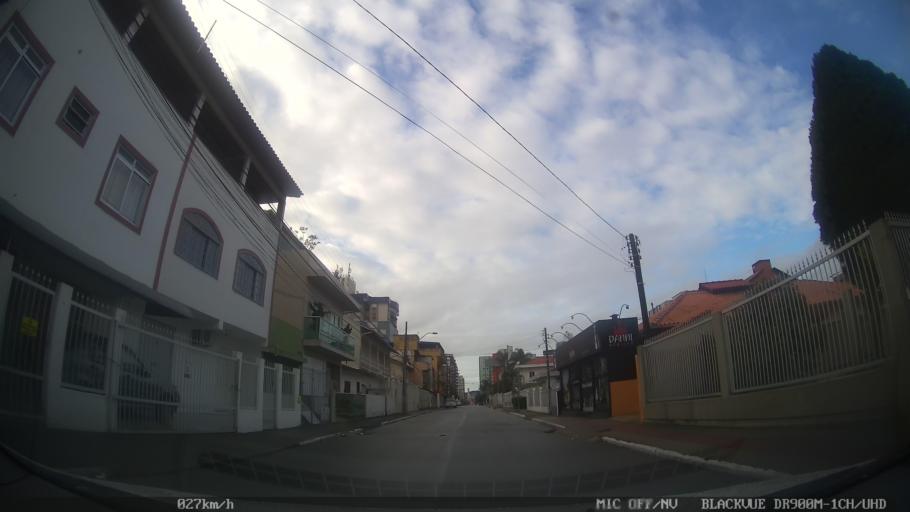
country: BR
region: Santa Catarina
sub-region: Sao Jose
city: Campinas
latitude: -27.5907
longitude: -48.6110
